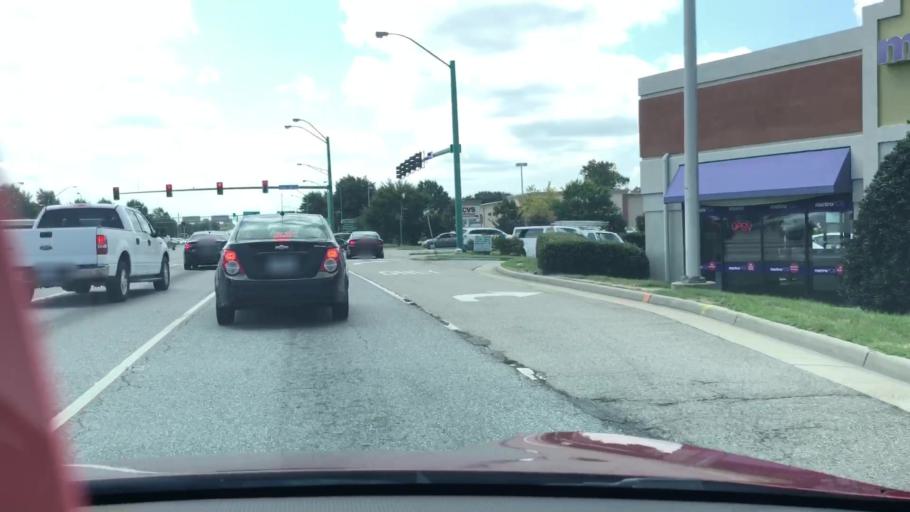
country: US
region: Virginia
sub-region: City of Chesapeake
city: Chesapeake
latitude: 36.8494
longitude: -76.2102
